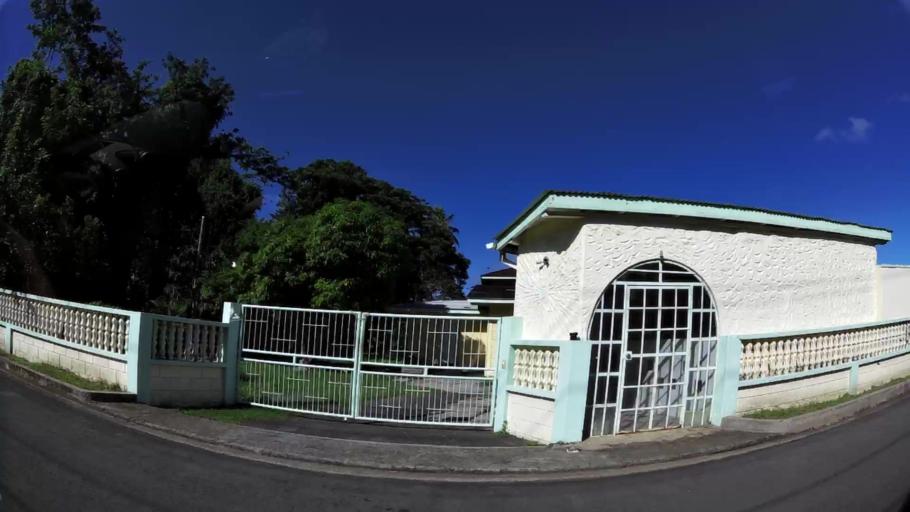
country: TT
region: Tobago
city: Scarborough
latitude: 11.1585
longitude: -60.8233
